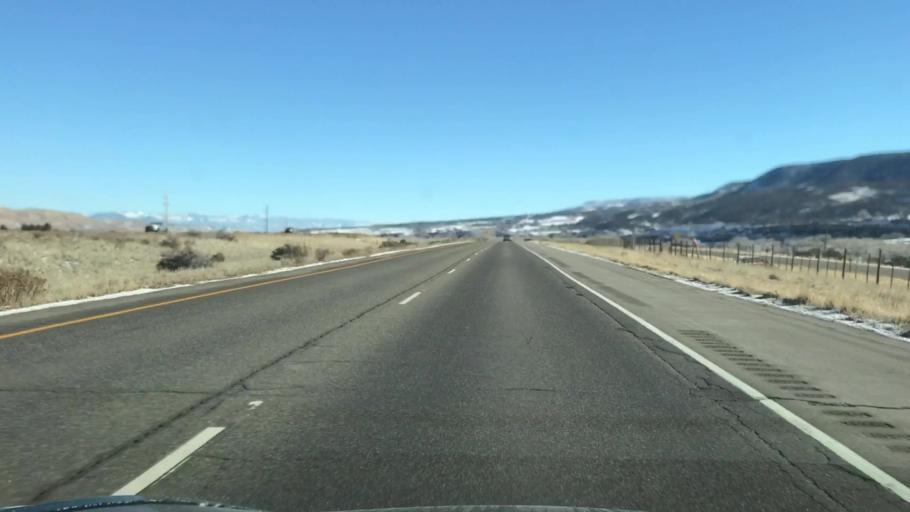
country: US
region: Colorado
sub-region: Garfield County
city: Battlement Mesa
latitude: 39.4776
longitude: -107.9809
